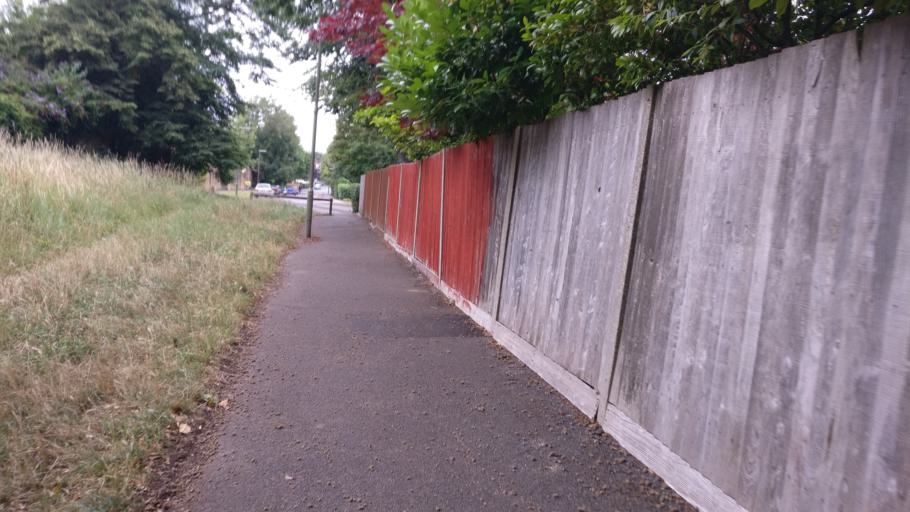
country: GB
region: England
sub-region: Surrey
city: Weybridge
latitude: 51.3741
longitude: -0.4474
